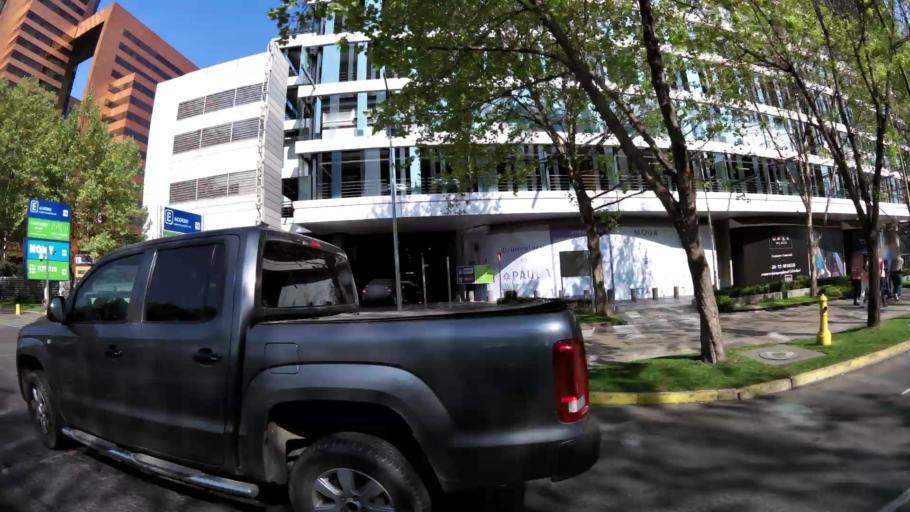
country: CL
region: Santiago Metropolitan
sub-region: Provincia de Santiago
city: Villa Presidente Frei, Nunoa, Santiago, Chile
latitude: -33.4004
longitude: -70.5753
